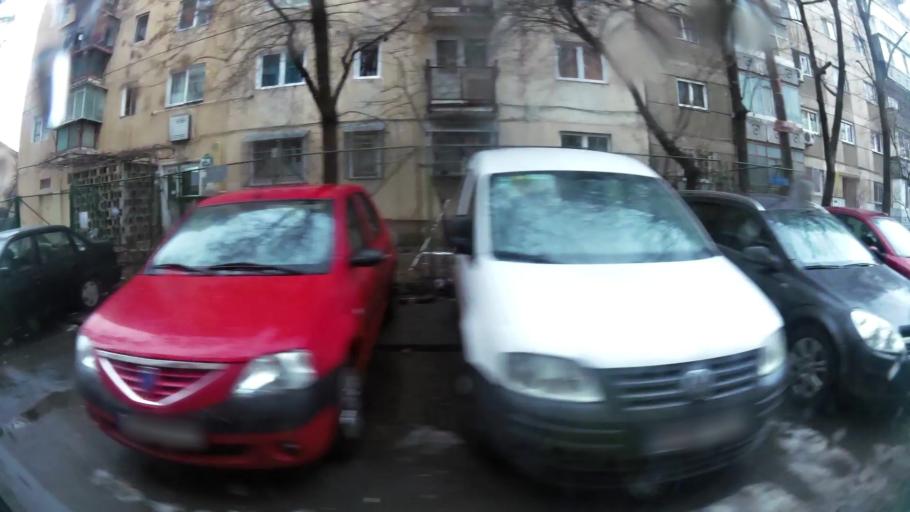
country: RO
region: Ilfov
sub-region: Comuna Chiajna
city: Rosu
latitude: 44.4315
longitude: 26.0145
